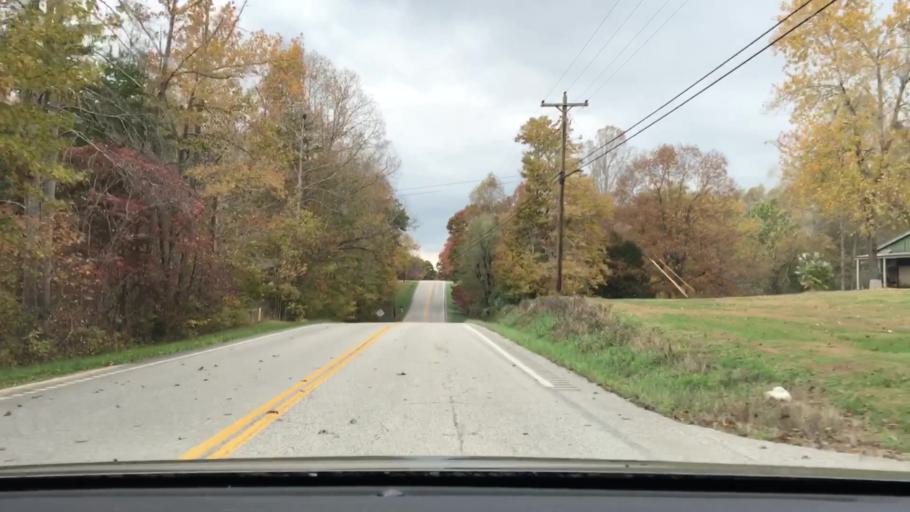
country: US
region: Tennessee
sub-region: Scott County
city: Huntsville
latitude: 36.3378
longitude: -84.6219
